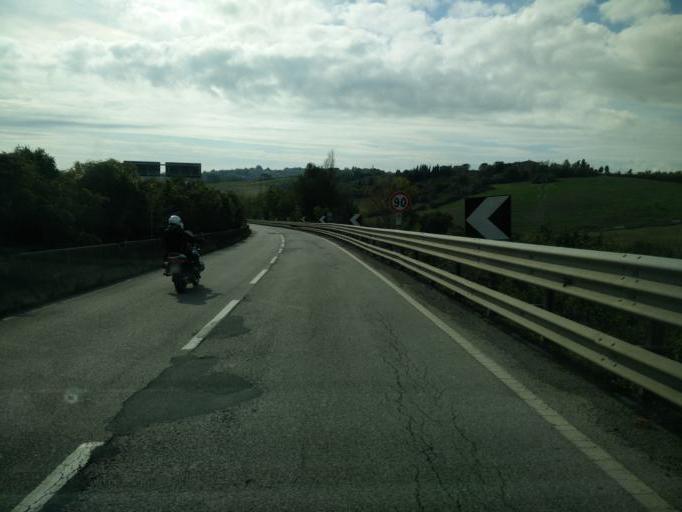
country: IT
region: Tuscany
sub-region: Provincia di Siena
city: Belverde
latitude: 43.3340
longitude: 11.2914
